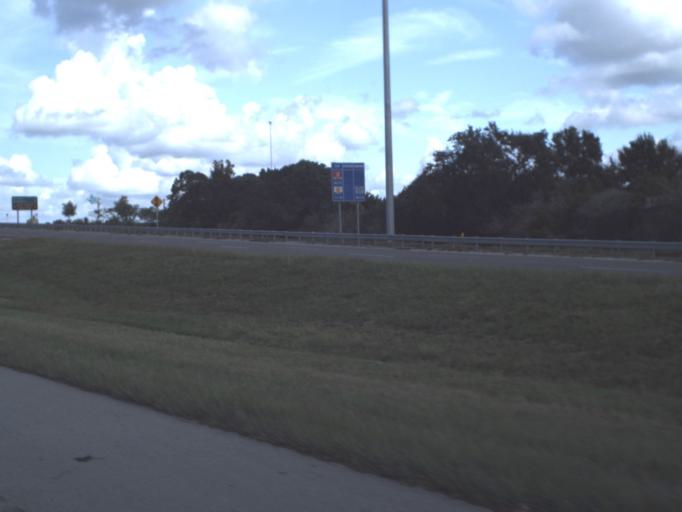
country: US
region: Florida
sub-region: Sarasota County
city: Nokomis
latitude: 27.1351
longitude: -82.4053
